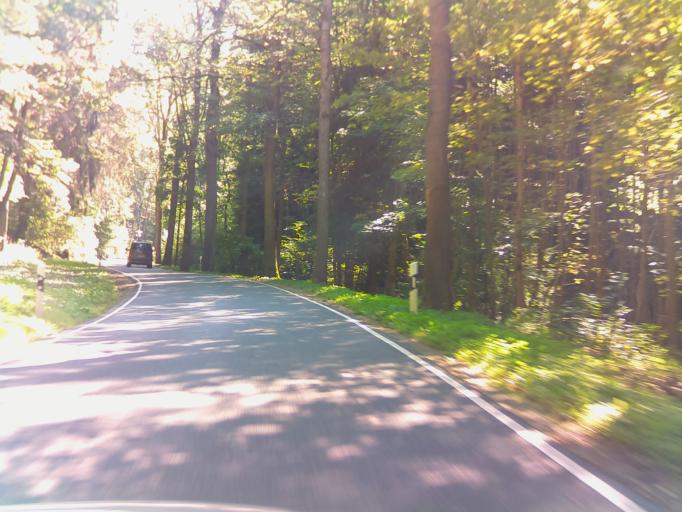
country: DE
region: Thuringia
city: Wurzbach
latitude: 50.5020
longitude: 11.4888
